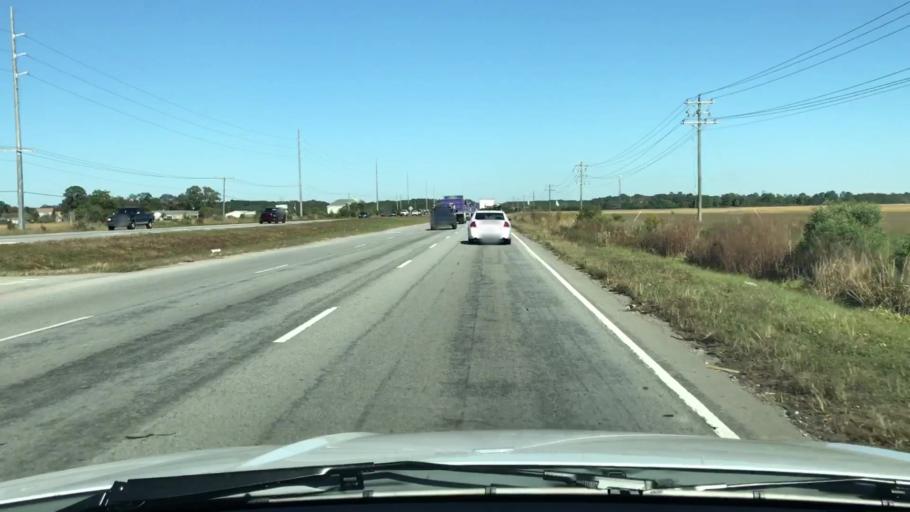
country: US
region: South Carolina
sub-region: Charleston County
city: Shell Point
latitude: 32.7927
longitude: -80.1404
